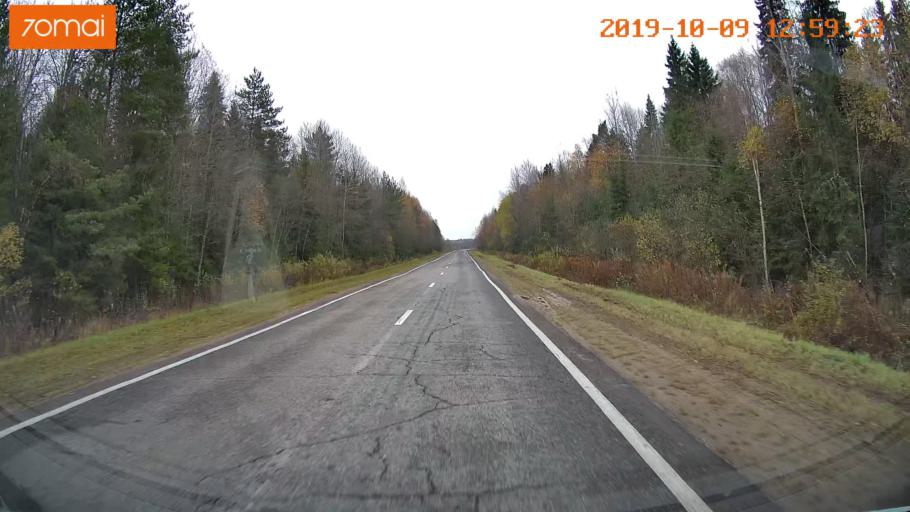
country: RU
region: Jaroslavl
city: Prechistoye
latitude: 58.3837
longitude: 40.4632
